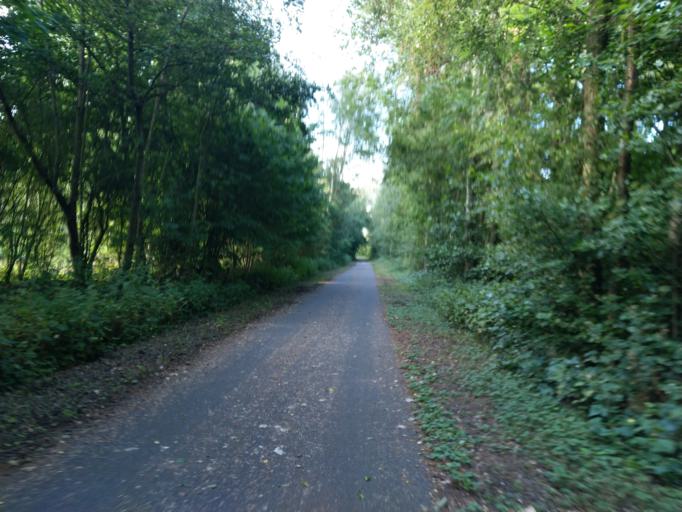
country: BE
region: Wallonia
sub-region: Province du Hainaut
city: Erquelinnes
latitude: 50.3356
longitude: 4.0999
